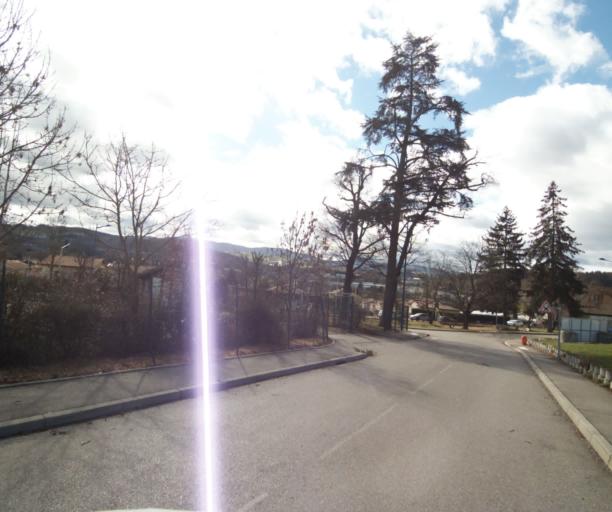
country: FR
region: Rhone-Alpes
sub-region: Departement de la Loire
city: La Talaudiere
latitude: 45.4797
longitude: 4.4218
